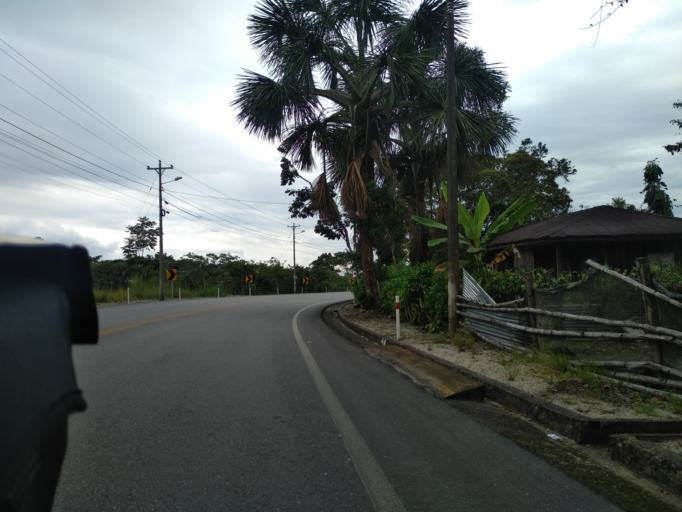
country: EC
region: Napo
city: Tena
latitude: -1.1924
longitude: -77.8766
